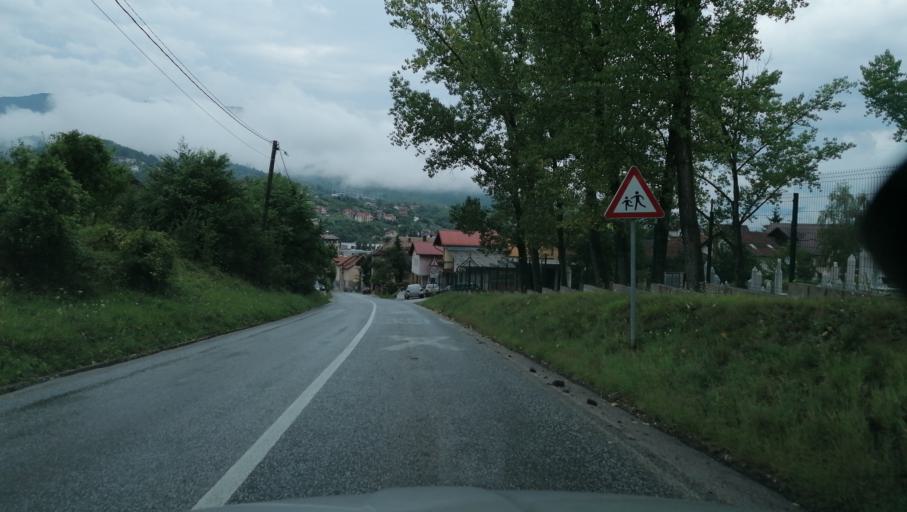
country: BA
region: Republika Srpska
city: Visegrad
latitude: 43.7840
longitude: 19.2992
